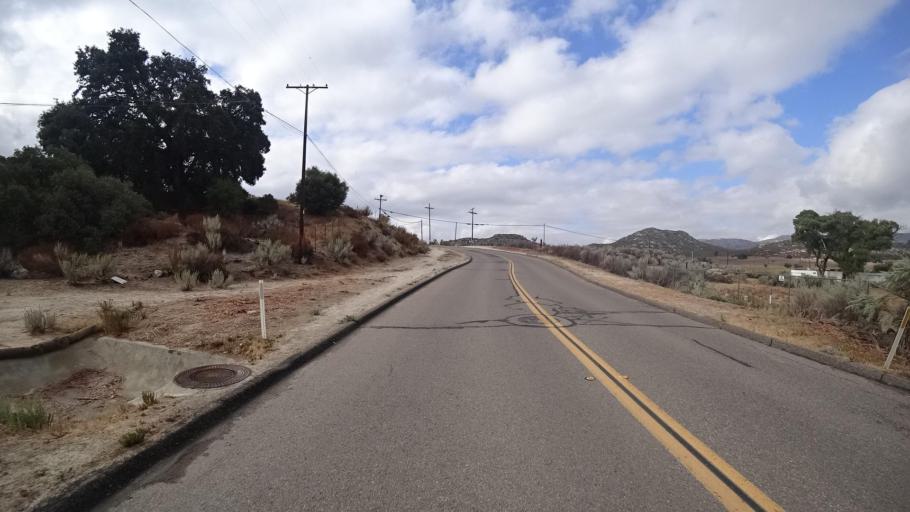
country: US
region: California
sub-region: San Diego County
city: Campo
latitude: 32.6156
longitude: -116.4698
